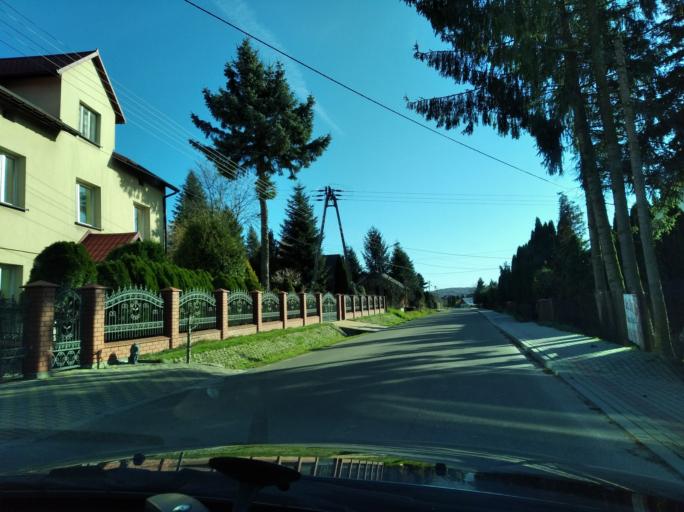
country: PL
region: Subcarpathian Voivodeship
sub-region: Powiat rzeszowski
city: Lutoryz
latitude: 49.9665
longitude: 21.9134
